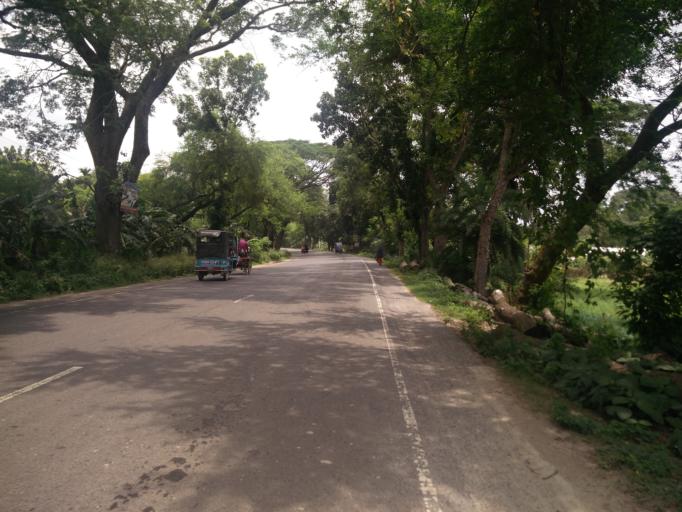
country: BD
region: Khulna
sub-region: Magura
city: Magura
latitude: 23.5433
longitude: 89.5342
